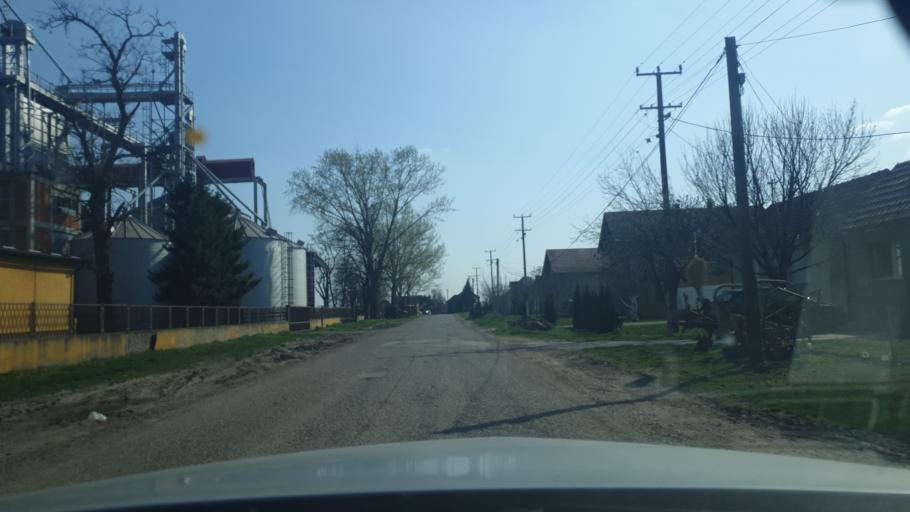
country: RS
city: Putinci
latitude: 45.0026
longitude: 19.9392
